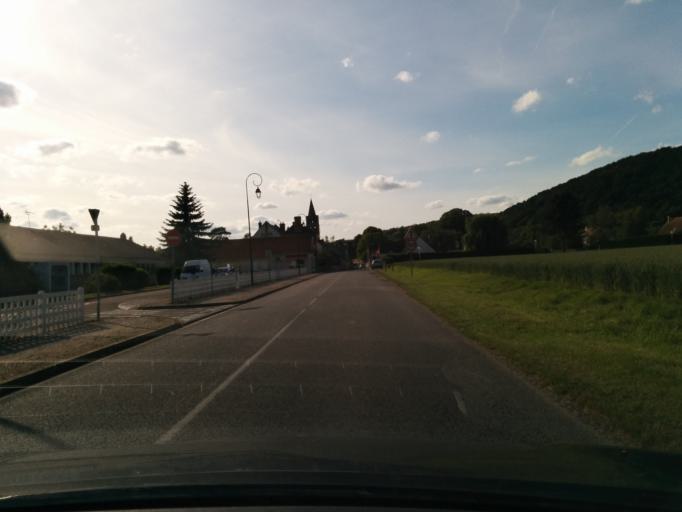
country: FR
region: Haute-Normandie
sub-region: Departement de l'Eure
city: Courcelles-sur-Seine
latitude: 49.1678
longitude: 1.4088
